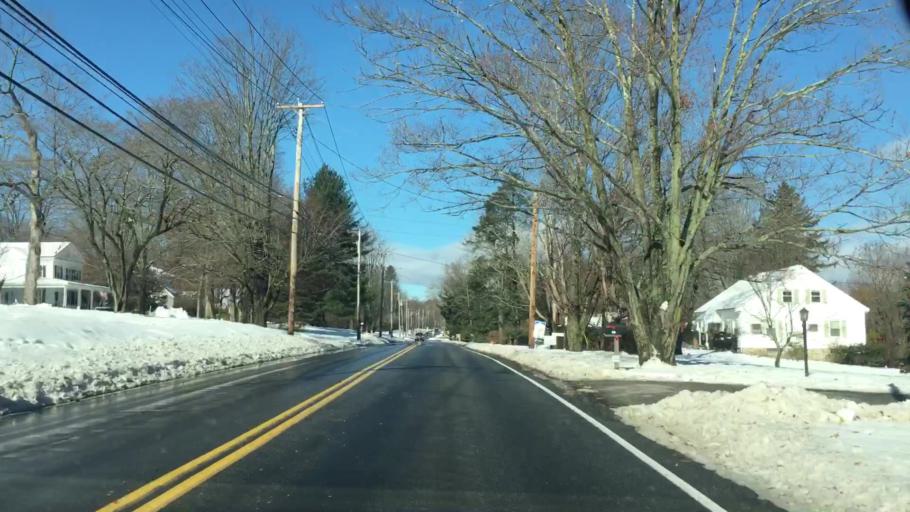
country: US
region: Connecticut
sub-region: Fairfield County
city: Shelton
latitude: 41.2900
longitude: -73.1422
